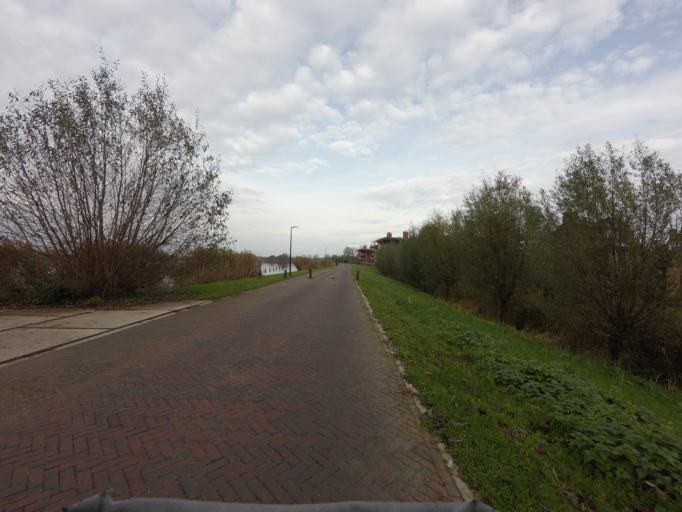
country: NL
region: North Holland
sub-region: Gemeente Amsterdam
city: Amsterdam-Zuidoost
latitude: 52.2766
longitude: 4.9676
